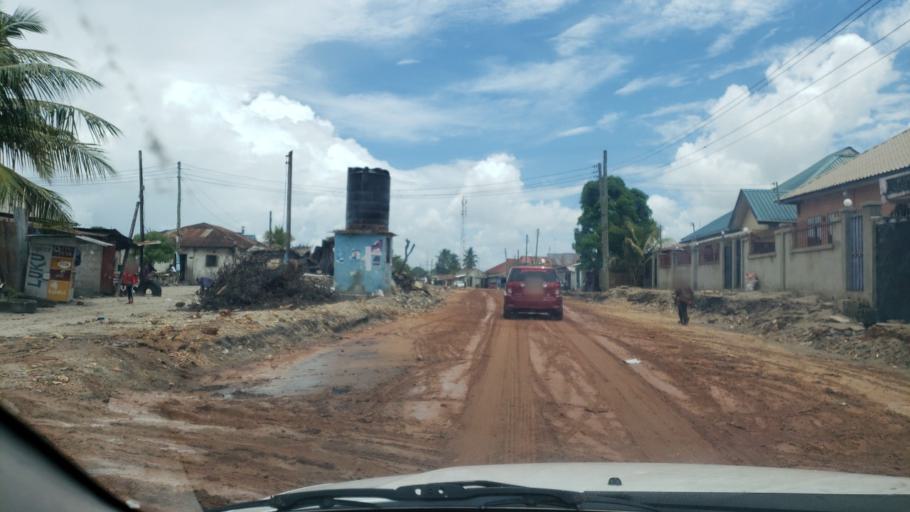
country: TZ
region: Dar es Salaam
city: Magomeni
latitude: -6.8113
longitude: 39.2529
